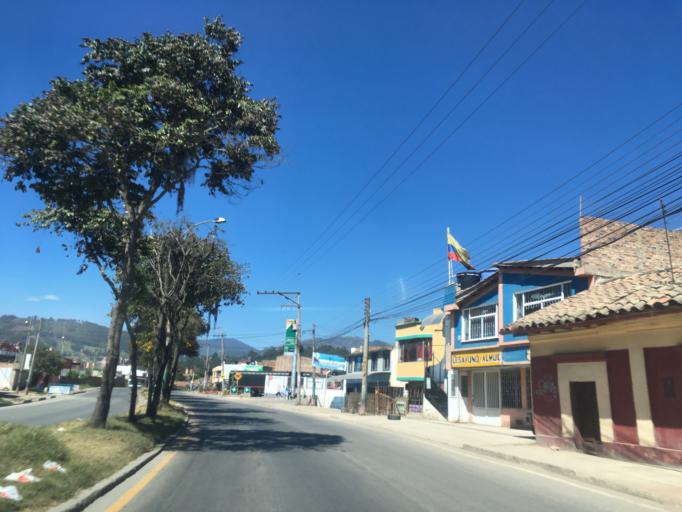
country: CO
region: Boyaca
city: Duitama
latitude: 5.8167
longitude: -73.0200
